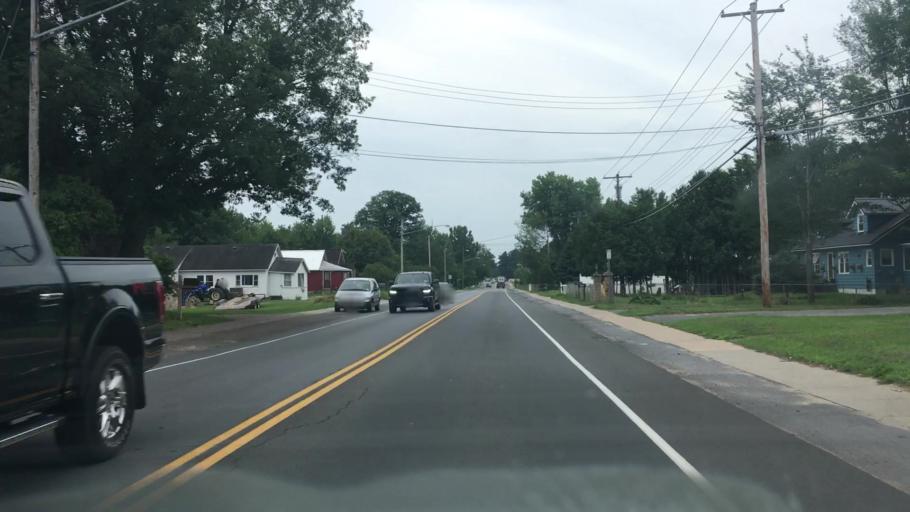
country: US
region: New York
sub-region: Clinton County
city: Plattsburgh West
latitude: 44.6807
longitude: -73.5062
